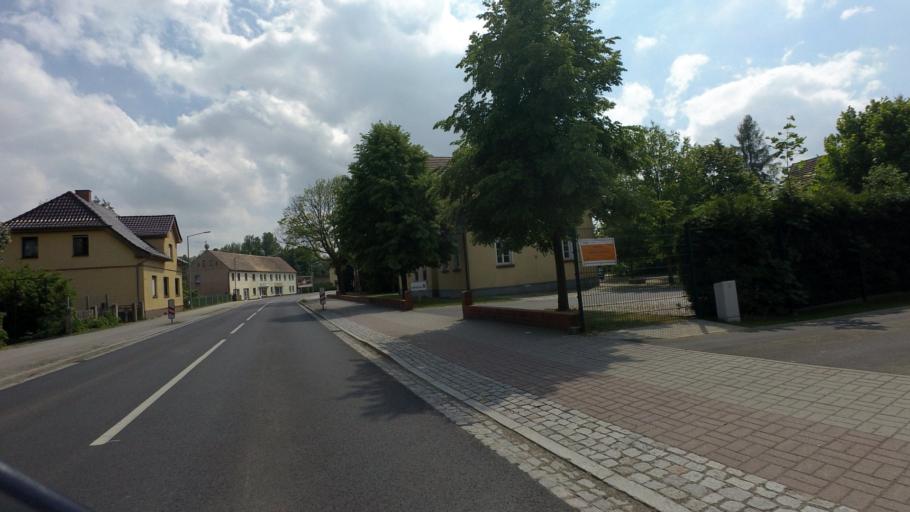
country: DE
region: Saxony
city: Rietschen
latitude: 51.3989
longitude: 14.7869
